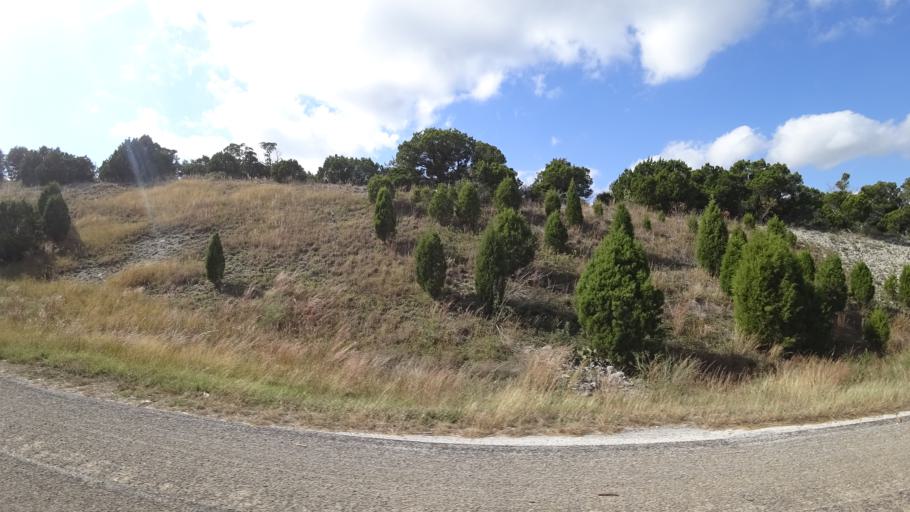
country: US
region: Texas
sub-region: Travis County
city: Barton Creek
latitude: 30.2658
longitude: -97.8934
